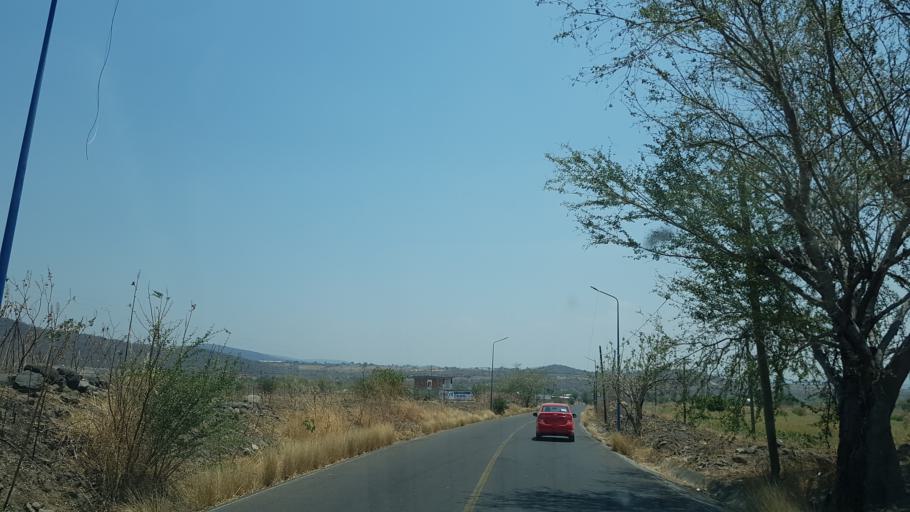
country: MX
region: Puebla
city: Huaquechula
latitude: 18.7658
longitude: -98.5319
